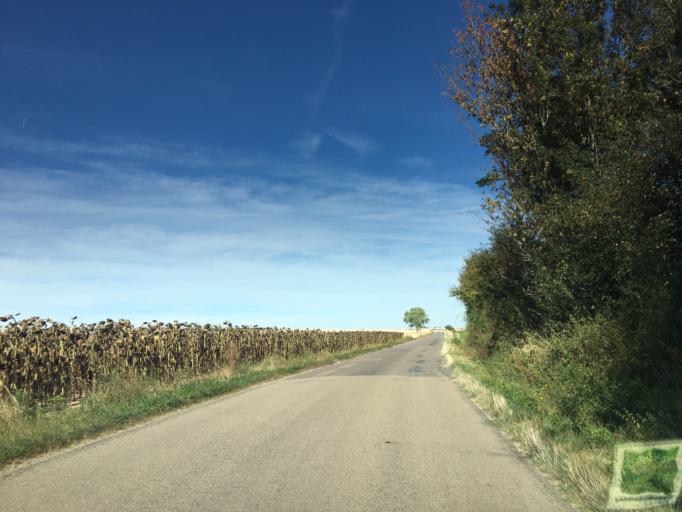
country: FR
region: Bourgogne
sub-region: Departement de l'Yonne
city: Fleury-la-Vallee
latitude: 47.8644
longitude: 3.4397
